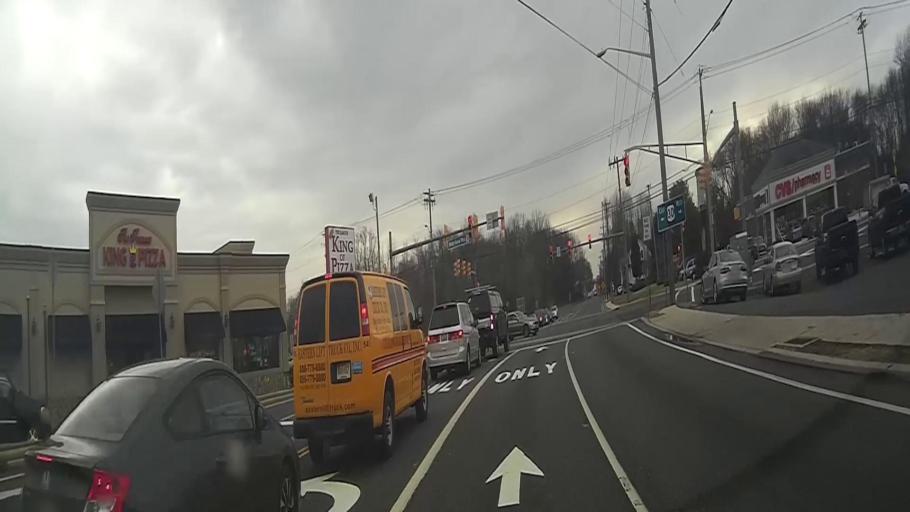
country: US
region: New Jersey
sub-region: Camden County
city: Berlin
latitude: 39.7976
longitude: -74.9330
